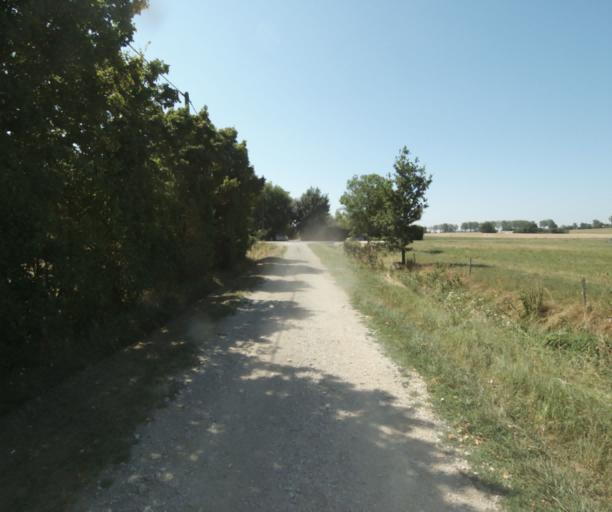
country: FR
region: Midi-Pyrenees
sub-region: Departement de la Haute-Garonne
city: Revel
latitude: 43.5069
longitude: 1.9613
